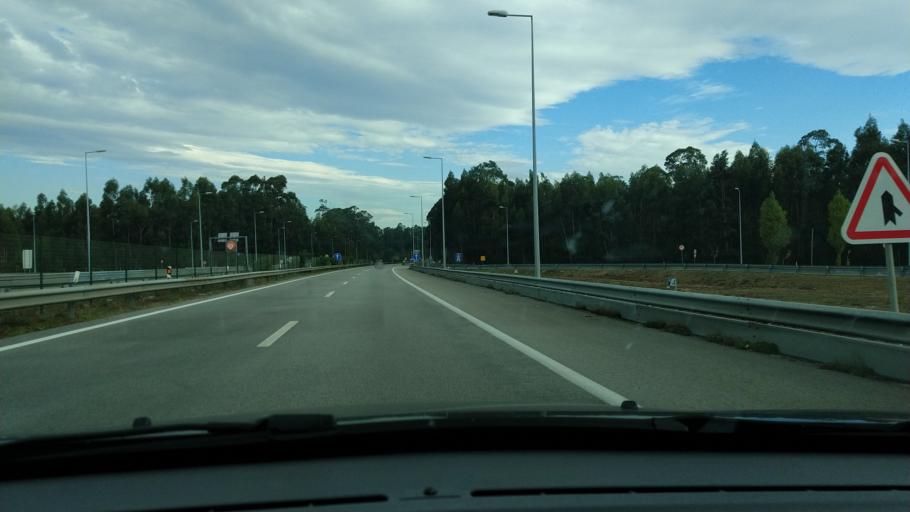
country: PT
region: Aveiro
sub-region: Aveiro
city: Eixo
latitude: 40.6612
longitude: -8.5918
